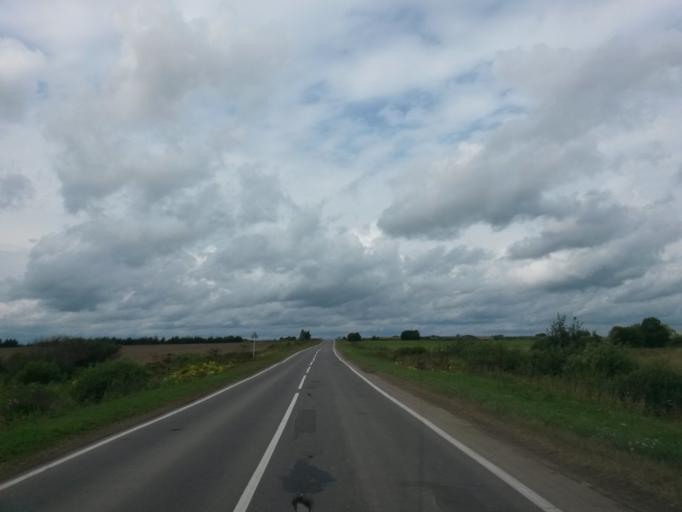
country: RU
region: Jaroslavl
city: Yaroslavl
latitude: 57.7477
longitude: 39.8812
